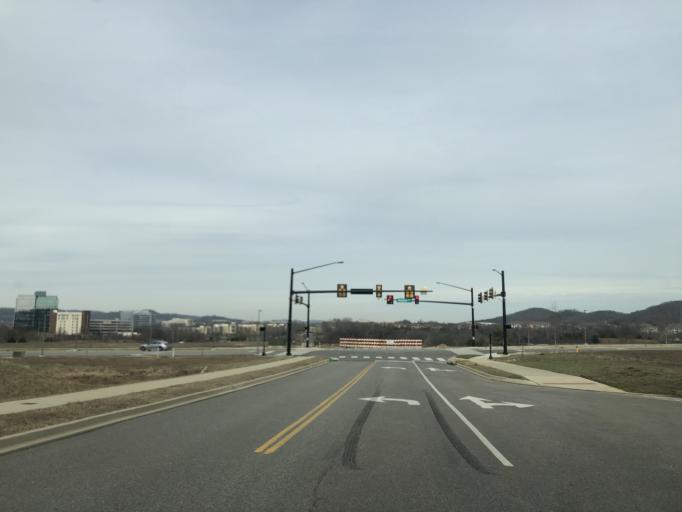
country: US
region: Tennessee
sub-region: Williamson County
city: Franklin
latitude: 35.9278
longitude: -86.8112
